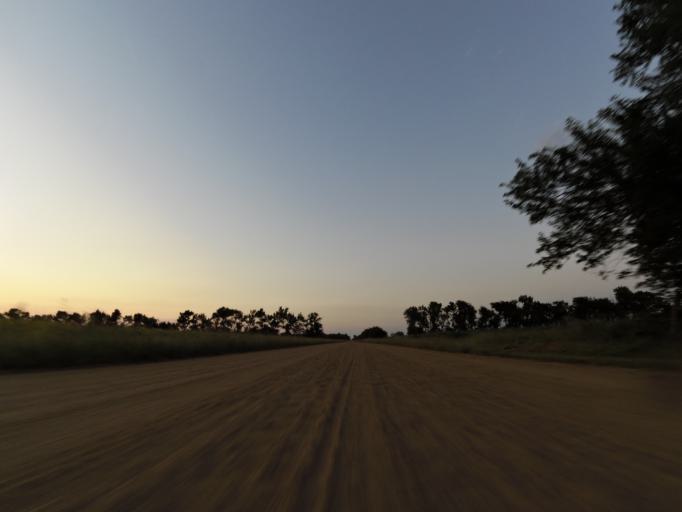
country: US
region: Kansas
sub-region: Reno County
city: South Hutchinson
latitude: 37.9615
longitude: -98.0319
